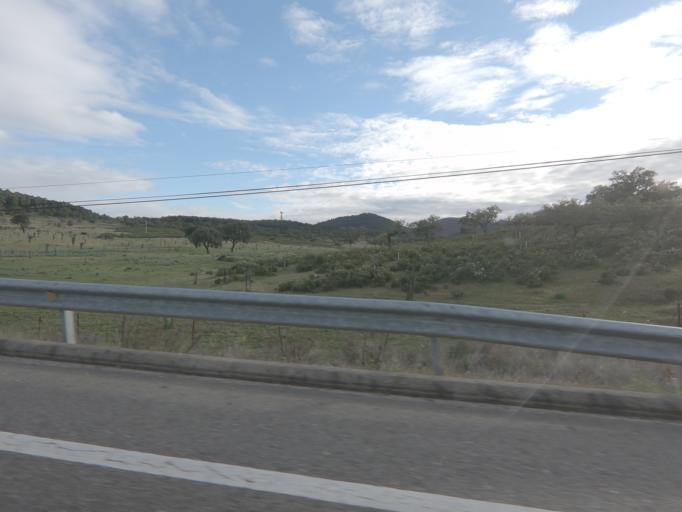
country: ES
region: Extremadura
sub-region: Provincia de Caceres
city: Canaveral
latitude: 39.8232
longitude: -6.3707
